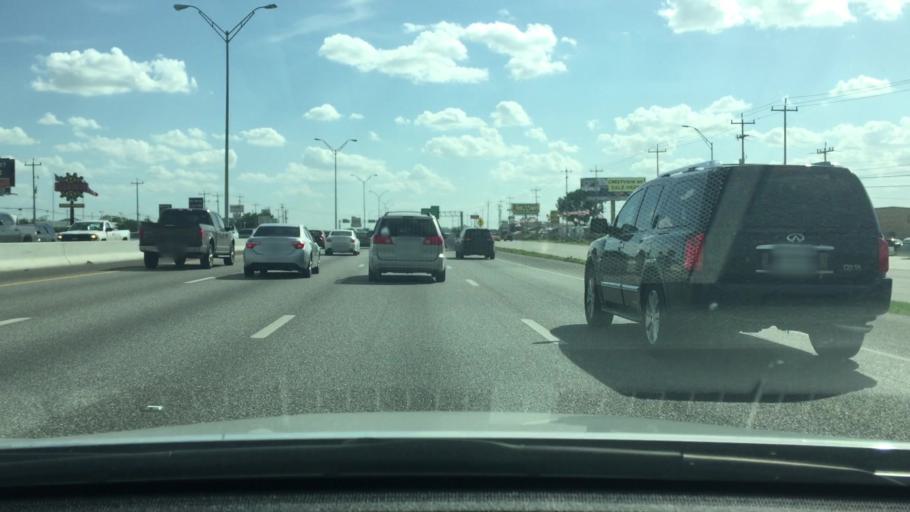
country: US
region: Texas
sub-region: Bexar County
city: Selma
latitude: 29.5906
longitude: -98.2962
